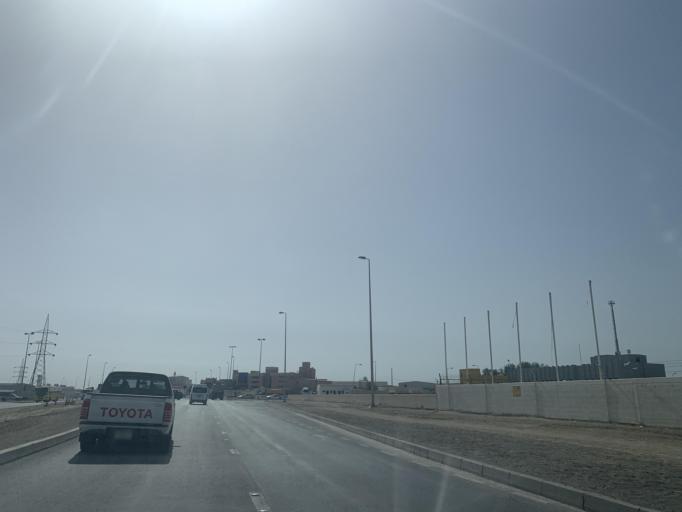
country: BH
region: Northern
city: Sitrah
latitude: 26.1774
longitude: 50.6113
